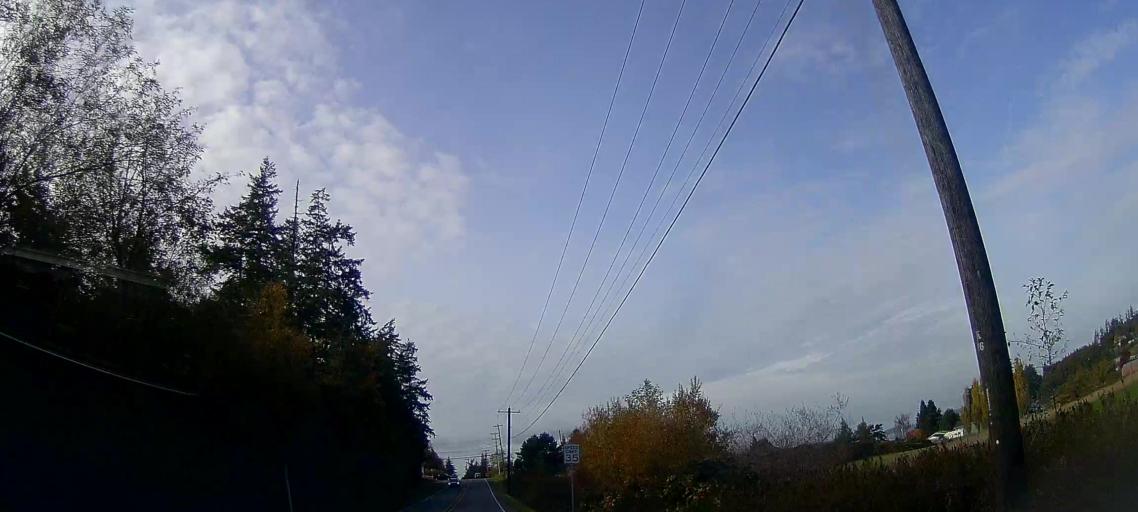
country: US
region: Washington
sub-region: Snohomish County
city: Stanwood
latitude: 48.2514
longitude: -122.4667
